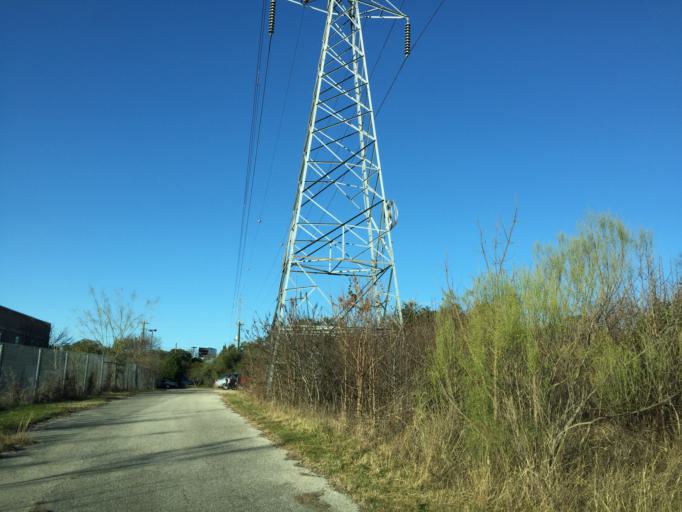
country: US
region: Texas
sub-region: Williamson County
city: Jollyville
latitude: 30.4040
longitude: -97.7413
